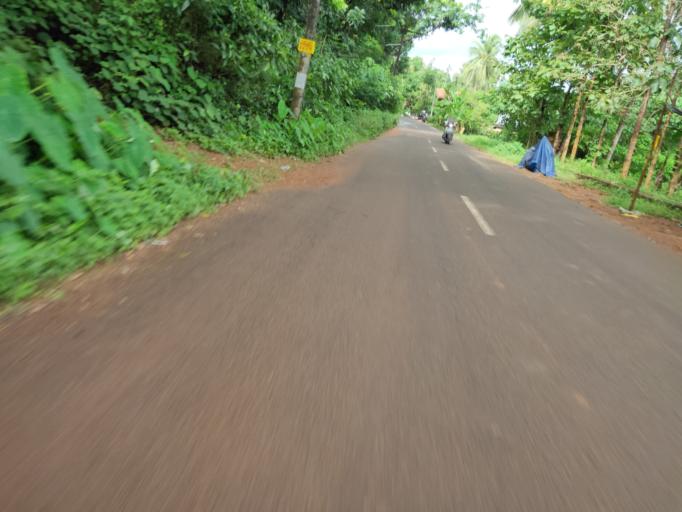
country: IN
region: Kerala
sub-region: Malappuram
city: Manjeri
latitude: 11.1442
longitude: 76.1374
